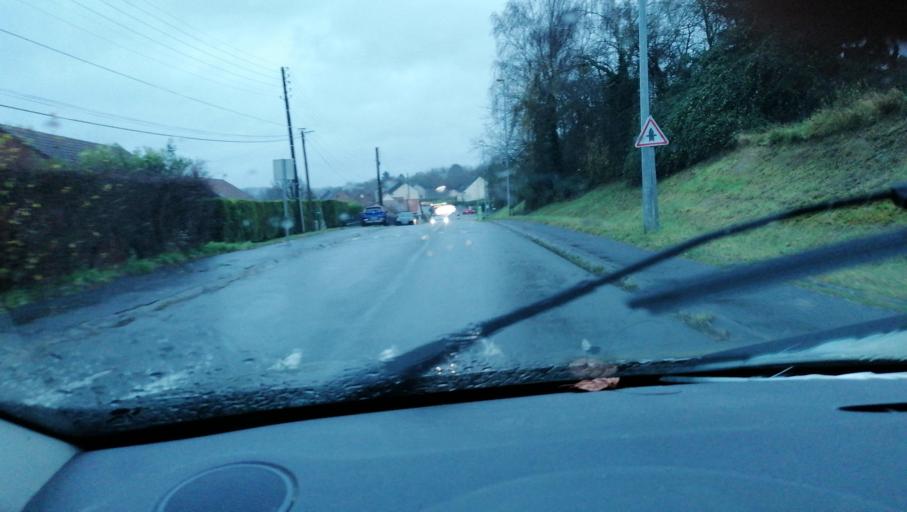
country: FR
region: Nord-Pas-de-Calais
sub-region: Departement du Nord
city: Boussois
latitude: 50.2833
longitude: 4.0560
